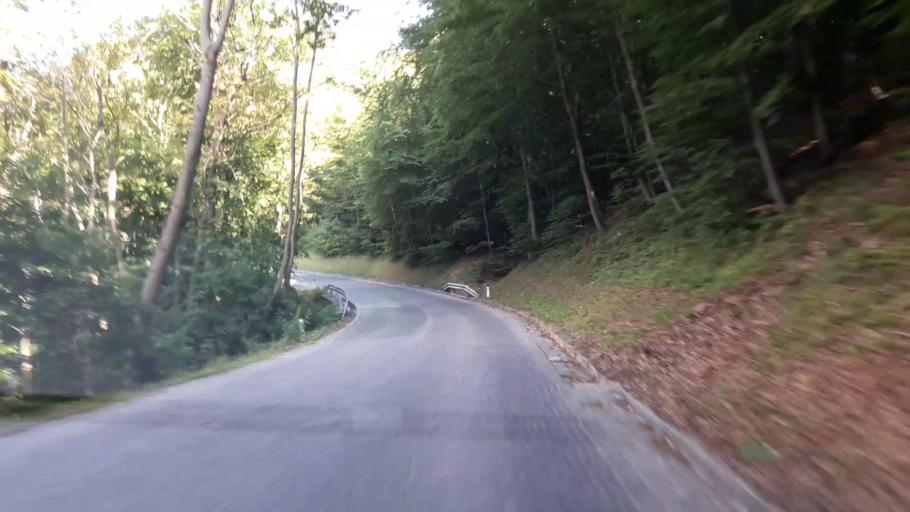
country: AT
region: Lower Austria
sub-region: Politischer Bezirk Wien-Umgebung
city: Klosterneuburg
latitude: 48.2802
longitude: 16.3271
